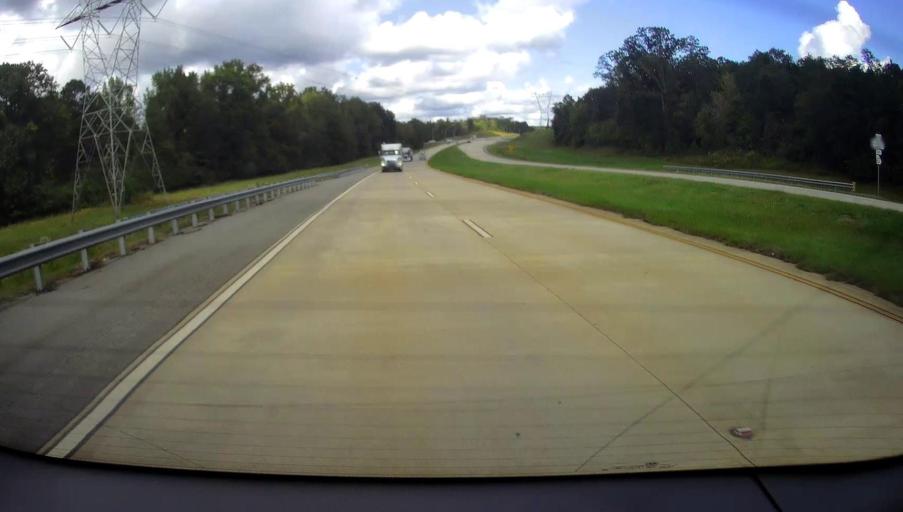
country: US
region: Georgia
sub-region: Jones County
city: Gray
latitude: 33.0150
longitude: -83.5693
